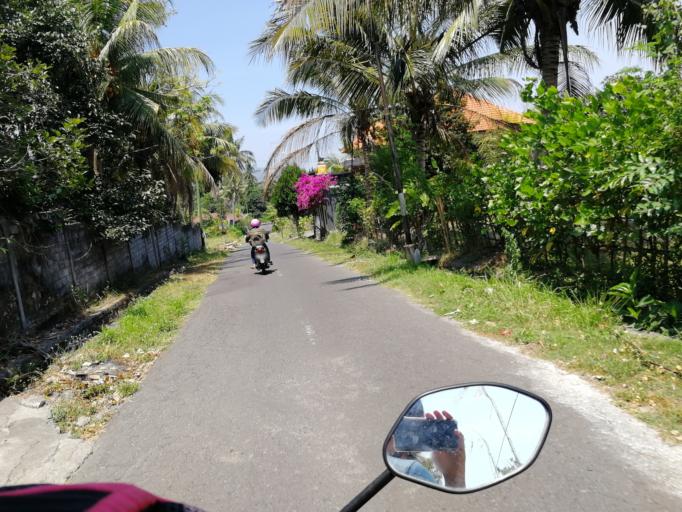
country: ID
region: Bali
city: Banjar Timbrah
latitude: -8.4662
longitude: 115.5932
